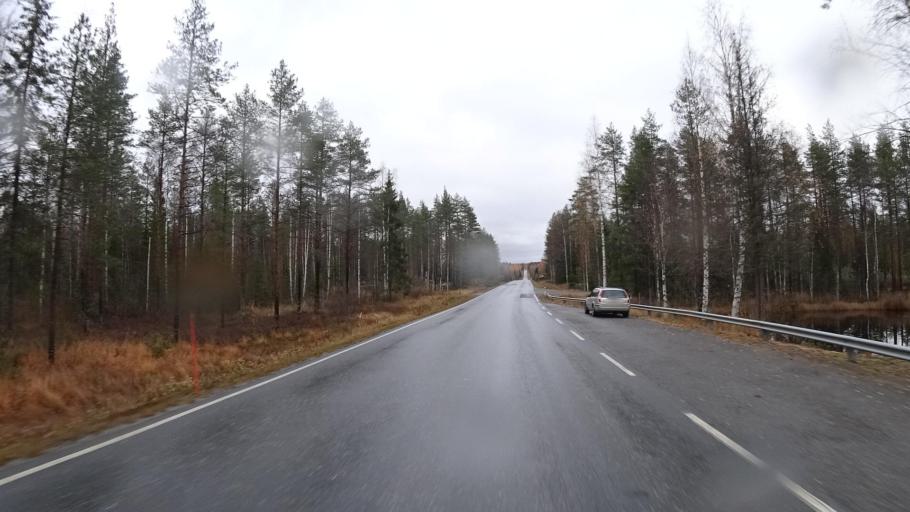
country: FI
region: North Karelia
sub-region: Joensuu
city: Polvijaervi
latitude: 63.0847
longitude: 29.5848
